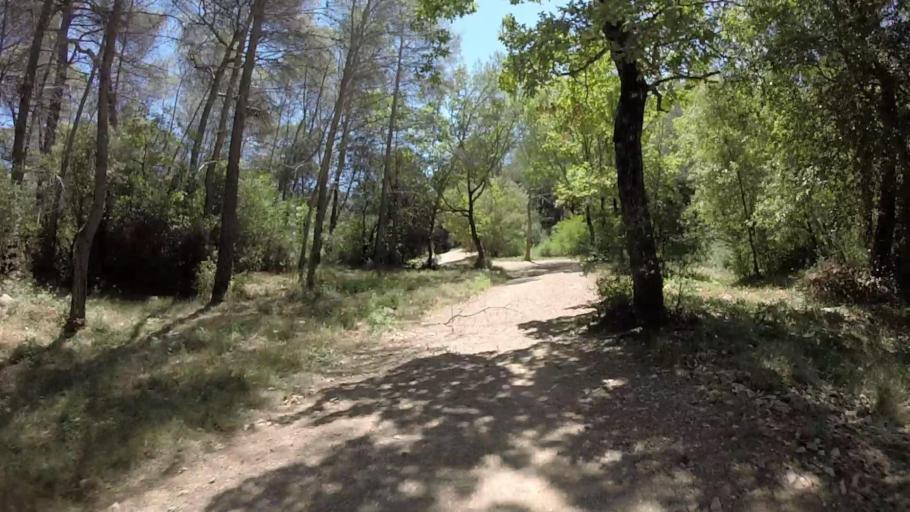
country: FR
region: Provence-Alpes-Cote d'Azur
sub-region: Departement des Alpes-Maritimes
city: Vallauris
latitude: 43.6075
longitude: 7.0385
